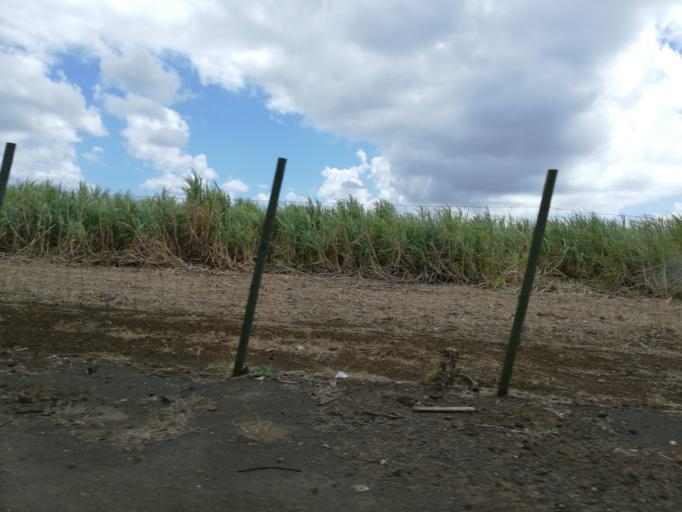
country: MU
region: Riviere du Rempart
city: Esperance Trebuchet
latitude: -20.0723
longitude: 57.6649
